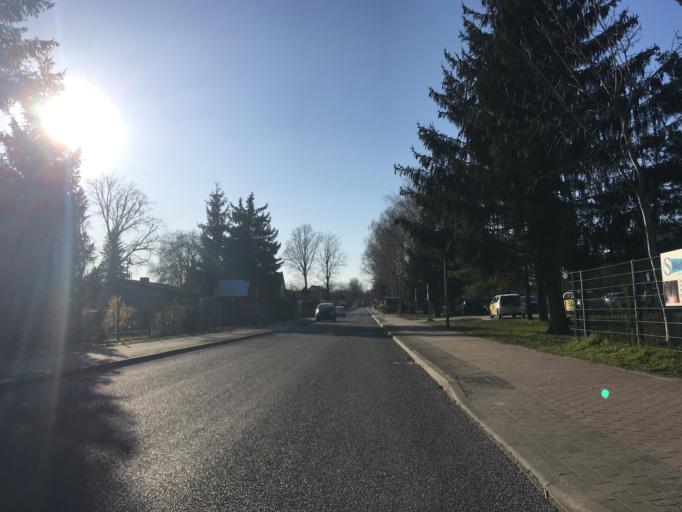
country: DE
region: Berlin
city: Buch
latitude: 52.6379
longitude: 13.5272
